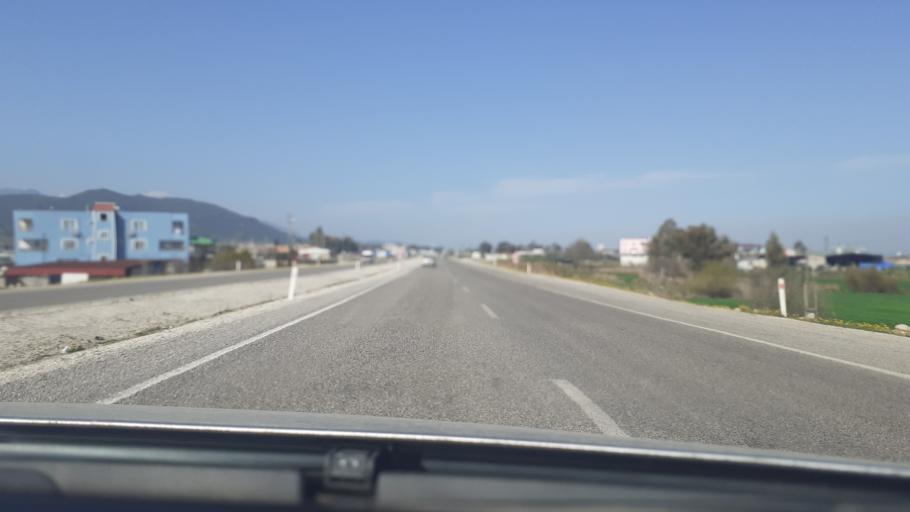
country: TR
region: Hatay
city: Aktepe
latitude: 36.6878
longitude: 36.4723
